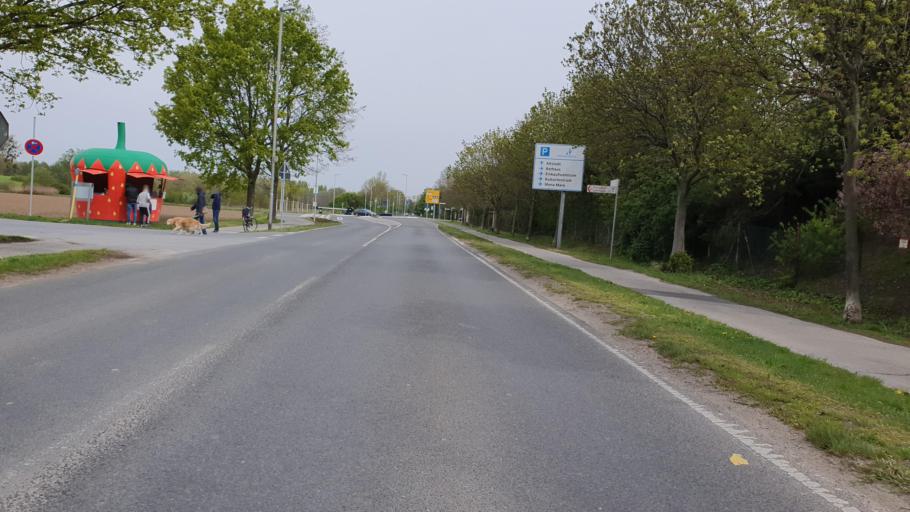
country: DE
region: North Rhine-Westphalia
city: Monheim am Rhein
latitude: 51.0810
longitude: 6.8835
